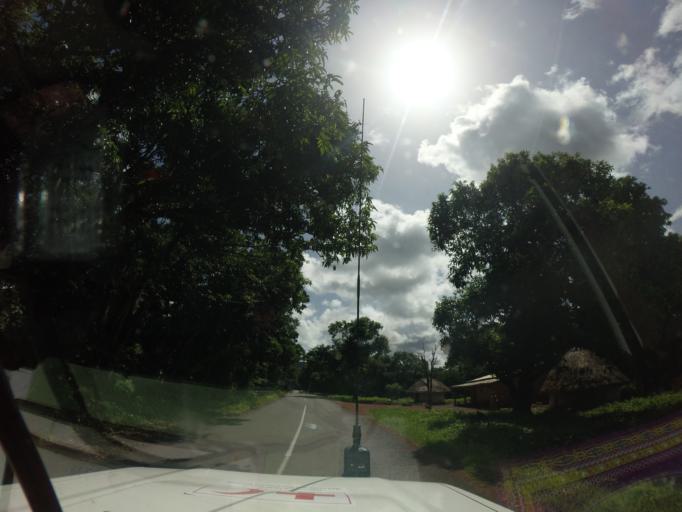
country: GN
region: Mamou
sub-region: Mamou Prefecture
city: Mamou
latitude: 10.2742
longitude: -11.9075
